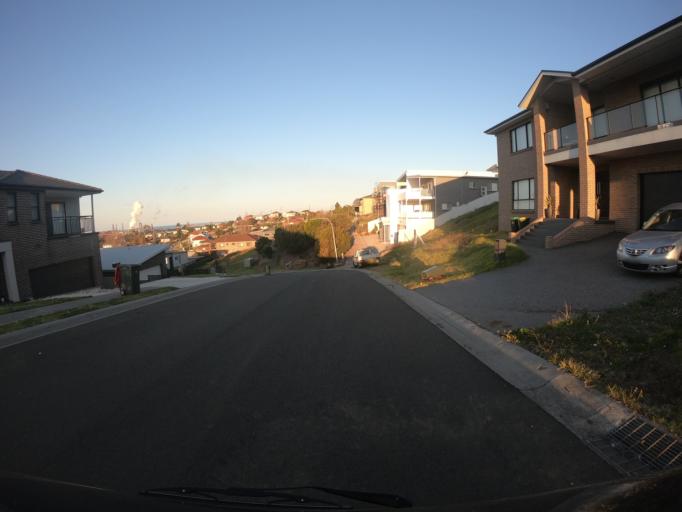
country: AU
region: New South Wales
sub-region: Wollongong
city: Lake Heights
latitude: -34.4781
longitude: 150.8679
